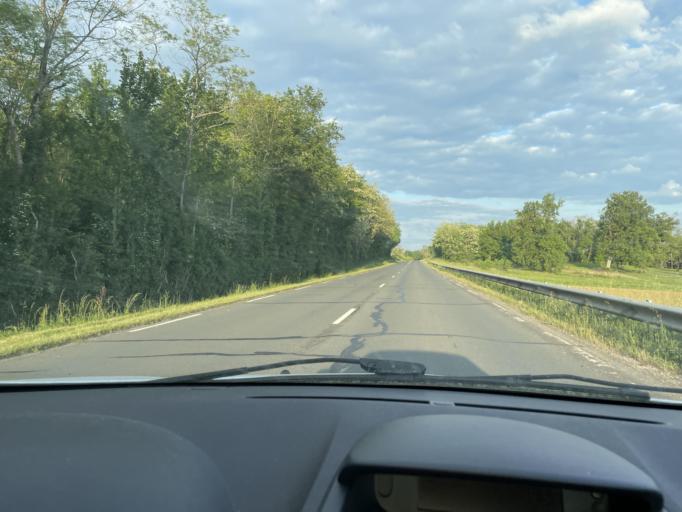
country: FR
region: Aquitaine
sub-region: Departement du Lot-et-Garonne
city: Casteljaloux
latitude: 44.3502
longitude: 0.0236
